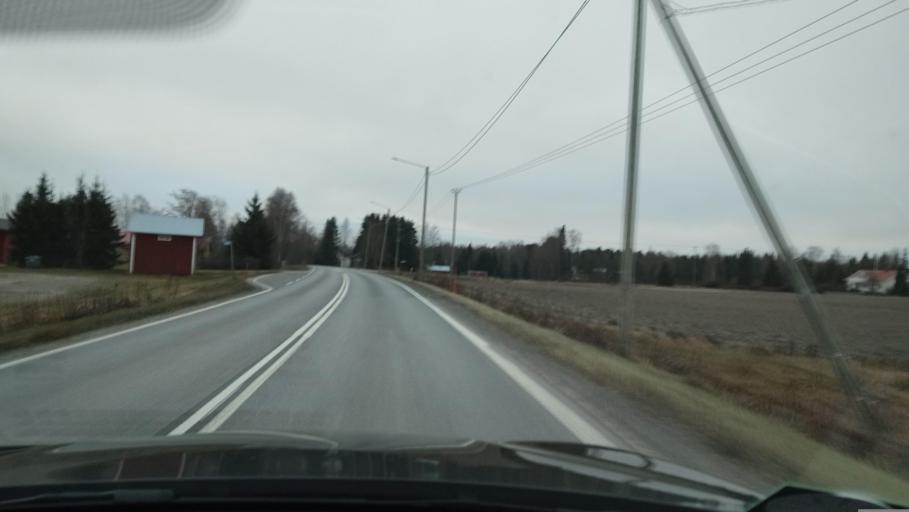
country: FI
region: Southern Ostrobothnia
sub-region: Suupohja
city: Karijoki
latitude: 62.3221
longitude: 21.7268
